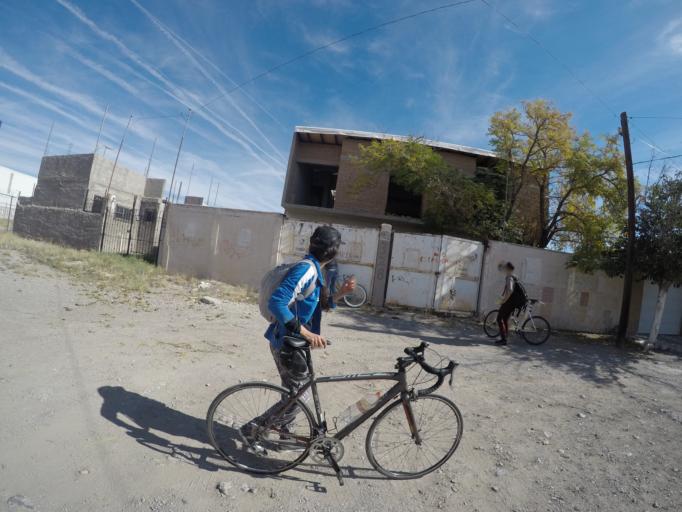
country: MX
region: Chihuahua
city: Ciudad Juarez
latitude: 31.7344
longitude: -106.4443
